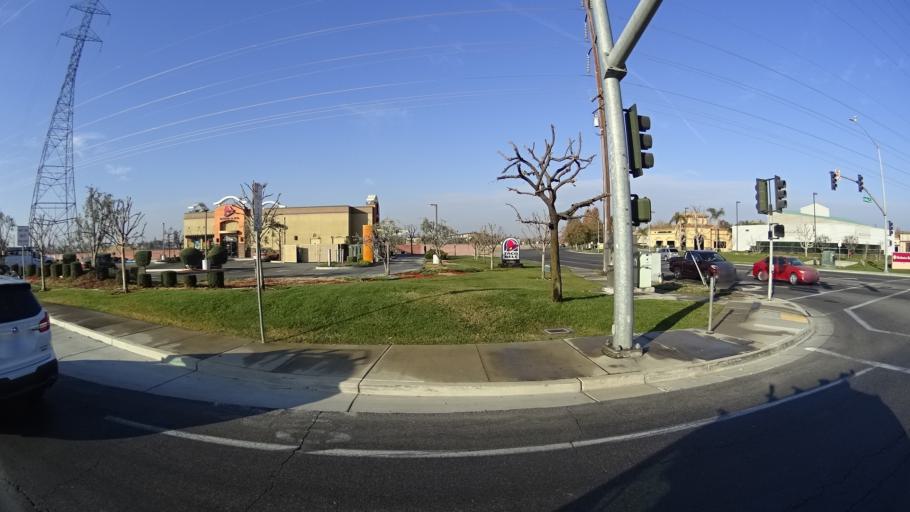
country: US
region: California
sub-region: Kern County
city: Greenacres
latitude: 35.3941
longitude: -119.0924
